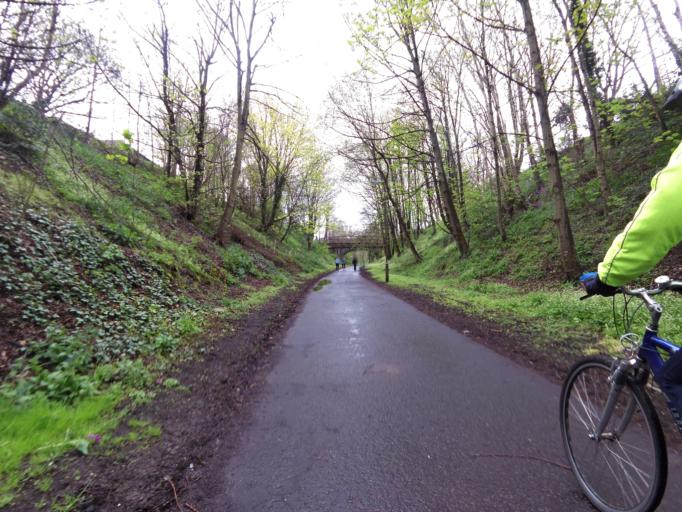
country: GB
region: Scotland
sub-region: Edinburgh
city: Edinburgh
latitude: 55.9500
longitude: -3.2347
